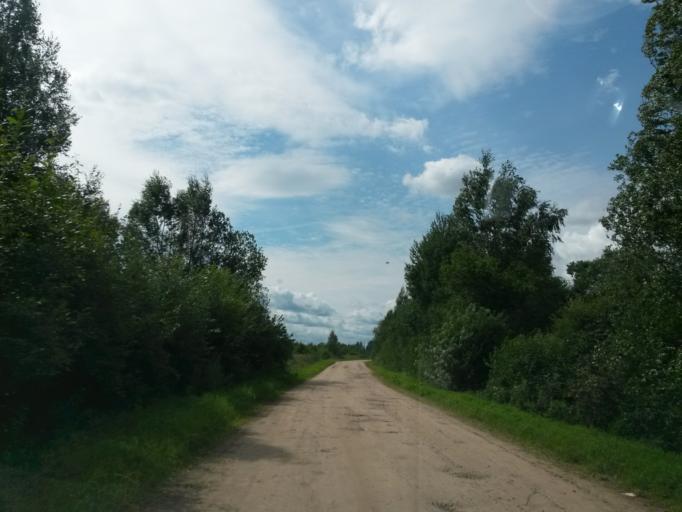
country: RU
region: Jaroslavl
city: Tutayev
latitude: 57.9483
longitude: 39.4574
